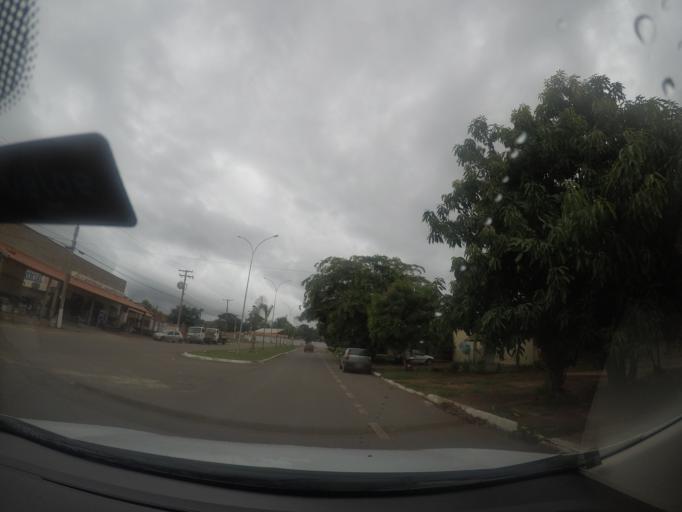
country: BR
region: Goias
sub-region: Trindade
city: Trindade
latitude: -16.6188
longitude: -49.3890
